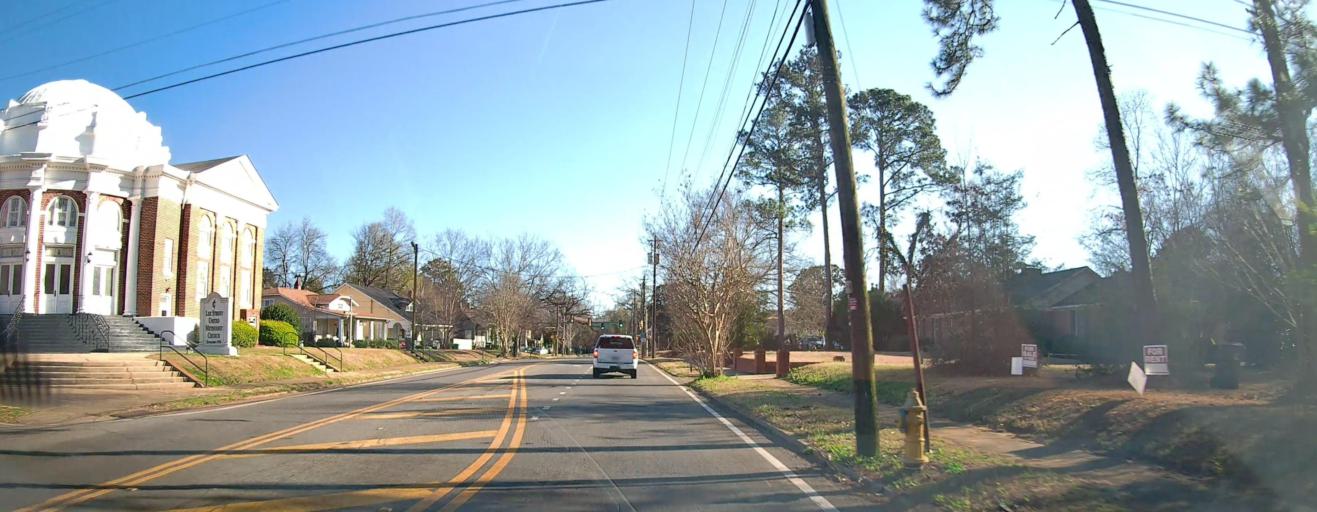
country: US
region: Georgia
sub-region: Sumter County
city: Americus
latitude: 32.0579
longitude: -84.2278
